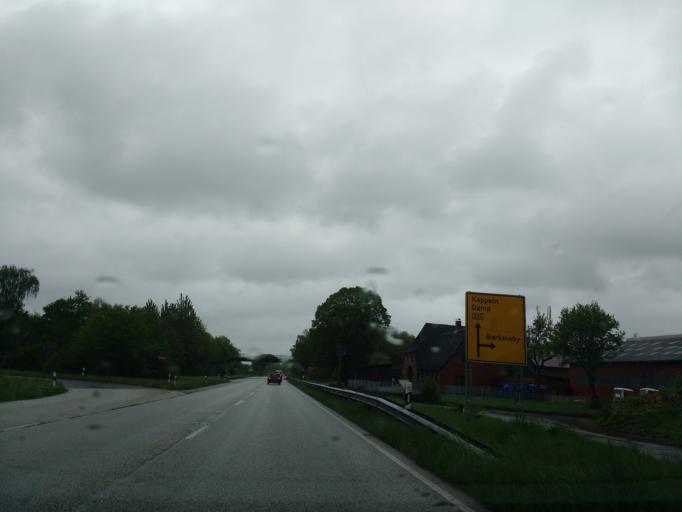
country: DE
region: Schleswig-Holstein
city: Barkelsby
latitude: 54.4984
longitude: 9.8460
